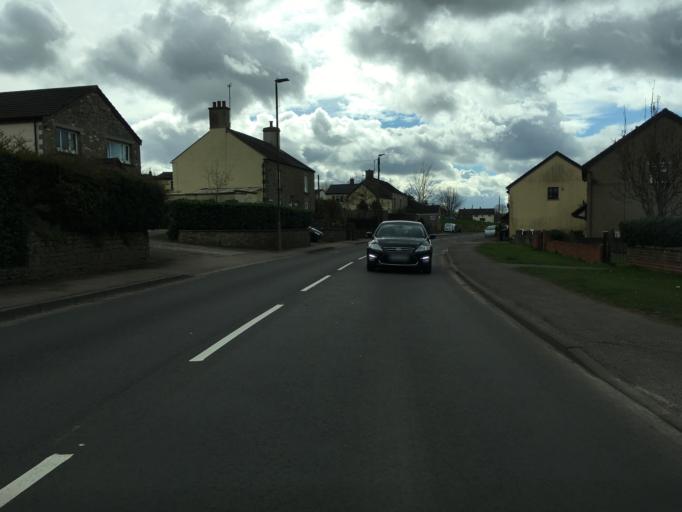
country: GB
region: England
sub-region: Gloucestershire
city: Coleford
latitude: 51.7967
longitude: -2.6110
